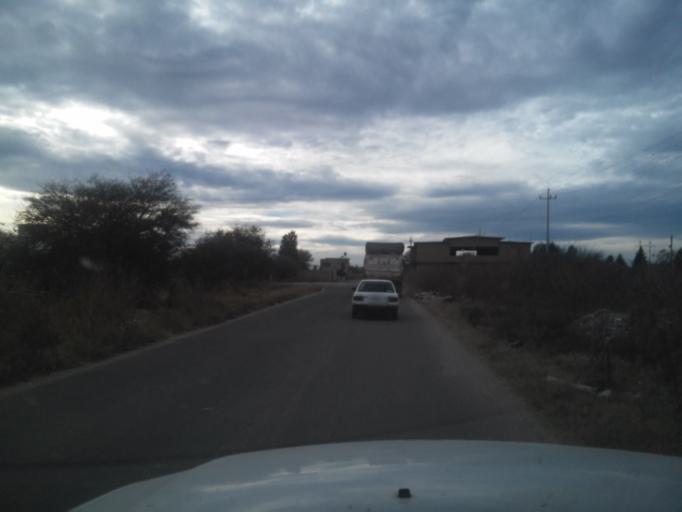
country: MX
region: Durango
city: Victoria de Durango
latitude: 24.0278
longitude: -104.5743
